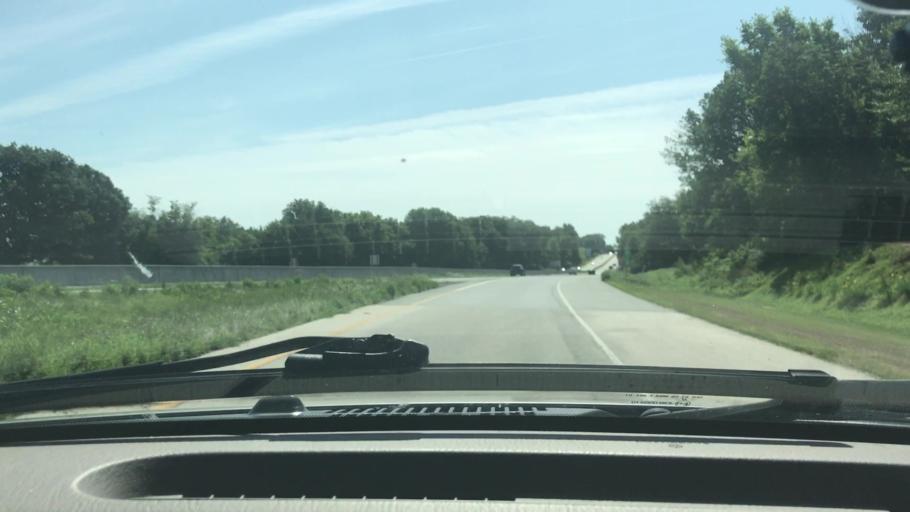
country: US
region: Pennsylvania
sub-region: Lancaster County
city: Salunga
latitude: 40.1112
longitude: -76.4430
